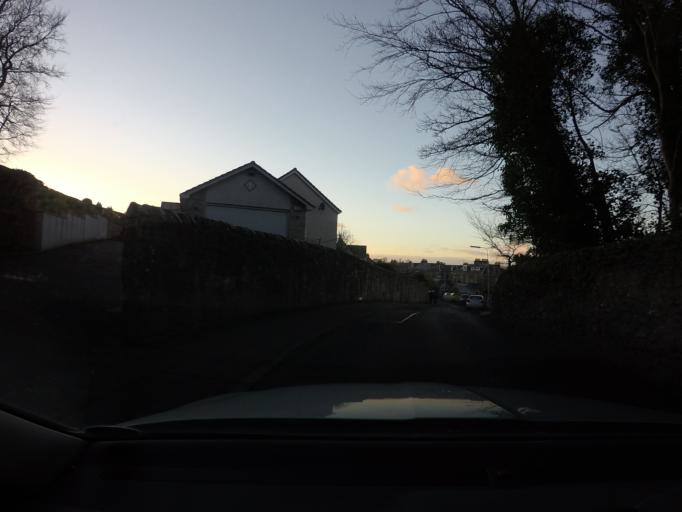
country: GB
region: Scotland
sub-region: Fife
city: Newport-On-Tay
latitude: 56.4333
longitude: -2.9446
